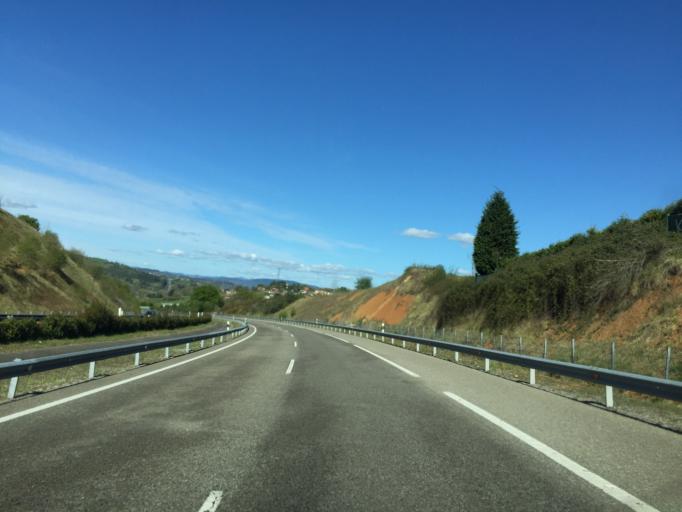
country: ES
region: Asturias
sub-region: Province of Asturias
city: Oviedo
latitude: 43.3527
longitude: -5.9112
